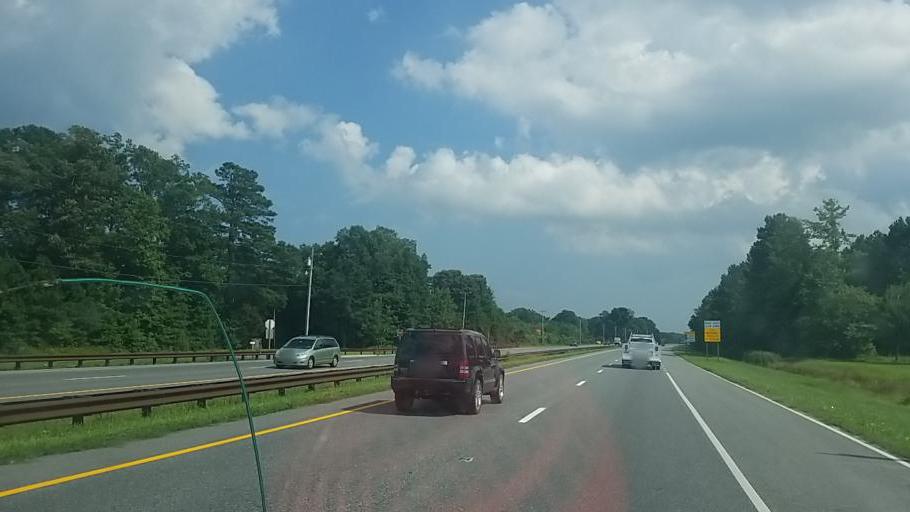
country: US
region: Delaware
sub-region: Sussex County
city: Selbyville
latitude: 38.4479
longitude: -75.2310
